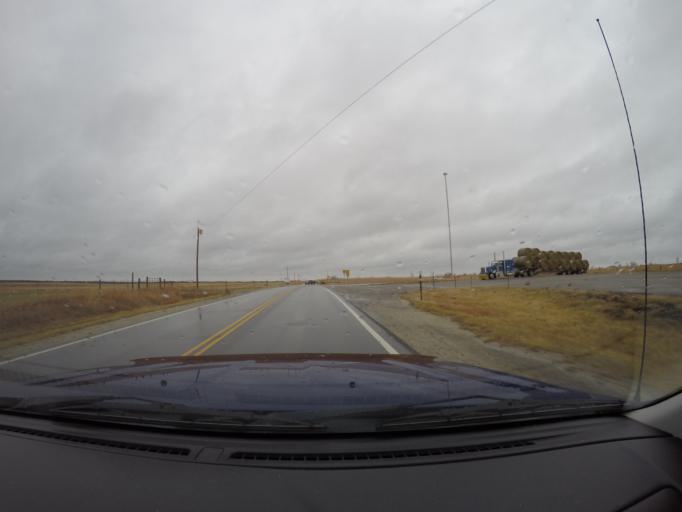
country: US
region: Kansas
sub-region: Pottawatomie County
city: Saint Marys
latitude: 39.4783
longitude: -96.0743
